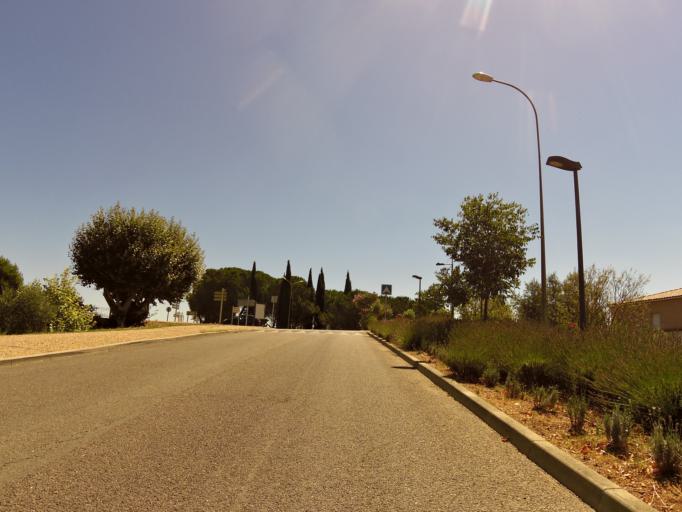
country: FR
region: Languedoc-Roussillon
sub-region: Departement du Gard
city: Vergeze
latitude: 43.7409
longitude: 4.2253
